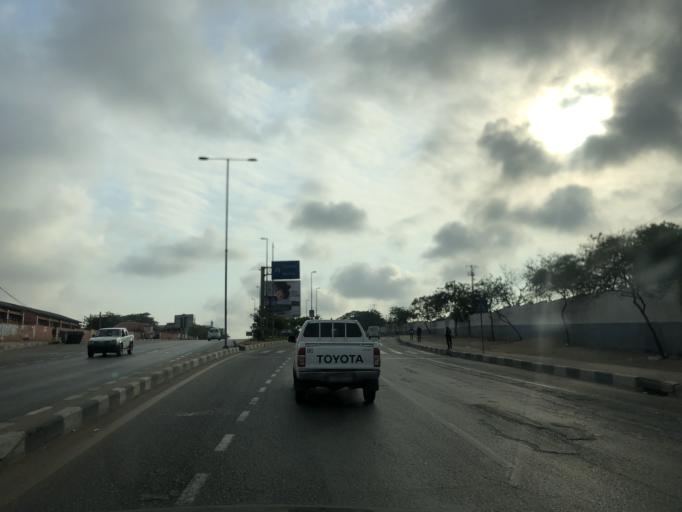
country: AO
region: Luanda
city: Luanda
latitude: -8.8498
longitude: 13.2241
